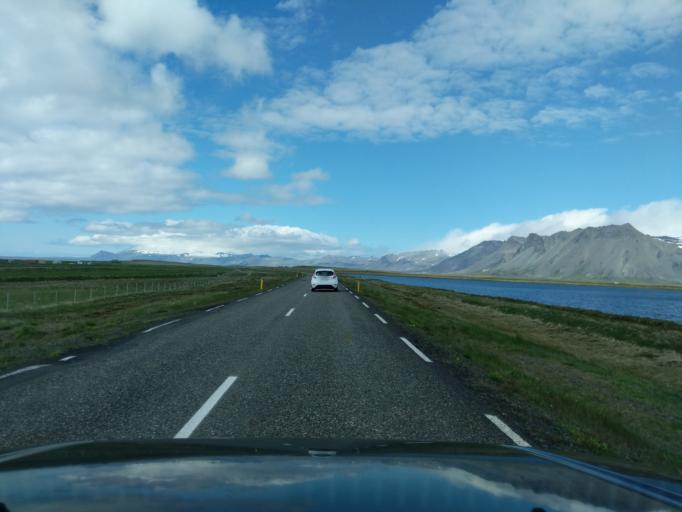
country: IS
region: West
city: Stykkisholmur
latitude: 64.8073
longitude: -23.0333
